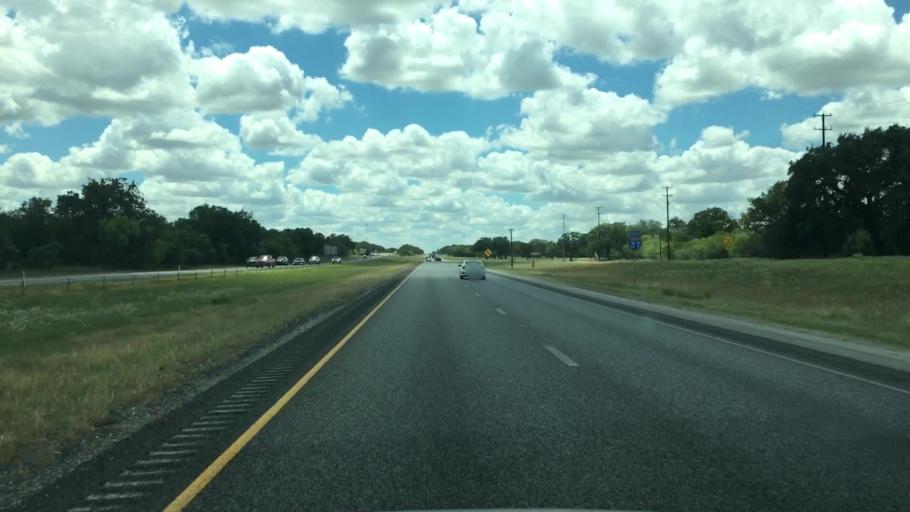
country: US
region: Texas
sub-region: Bexar County
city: Elmendorf
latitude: 29.2093
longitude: -98.4162
